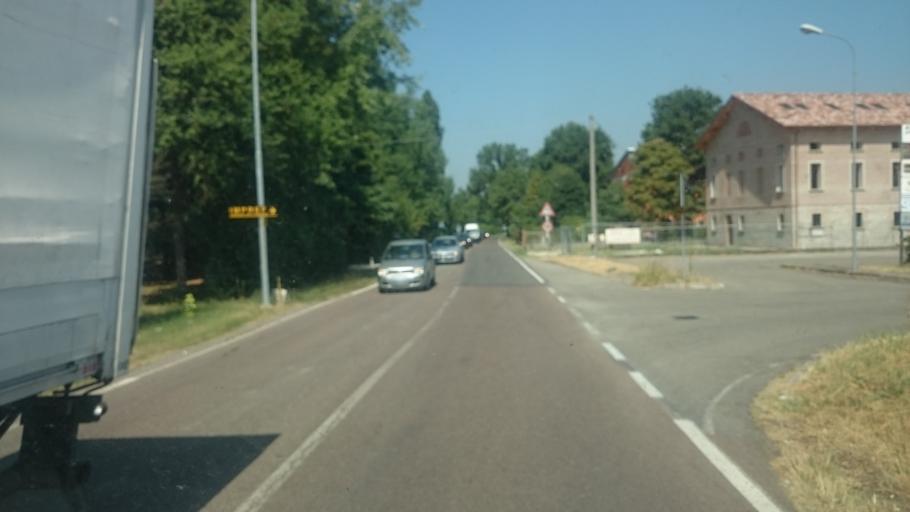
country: IT
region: Emilia-Romagna
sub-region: Provincia di Reggio Emilia
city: Arceto
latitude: 44.6248
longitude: 10.7149
